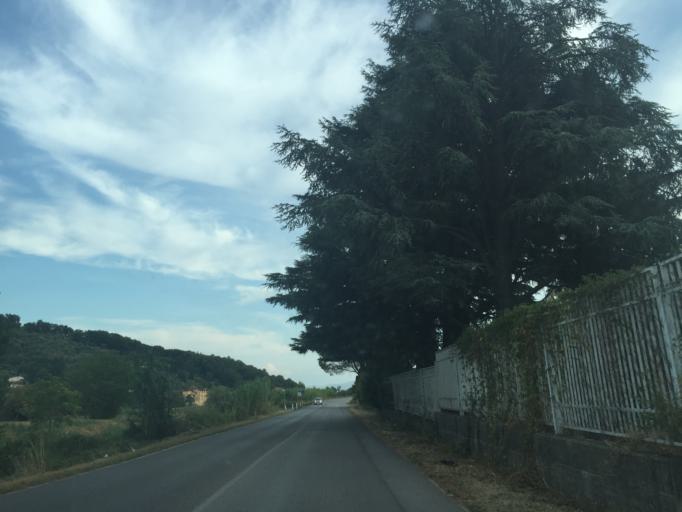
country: IT
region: Tuscany
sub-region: Provincia di Pistoia
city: Pistoia
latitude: 43.9653
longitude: 10.8939
